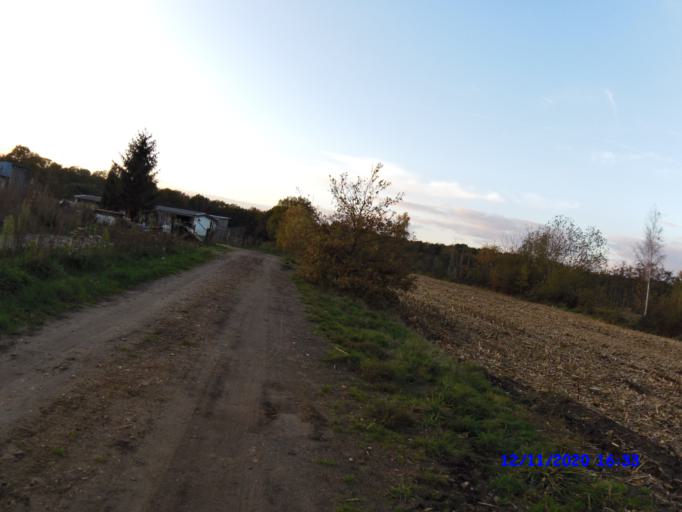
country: BE
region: Flanders
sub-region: Provincie Antwerpen
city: Meerhout
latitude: 51.1890
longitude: 5.0502
